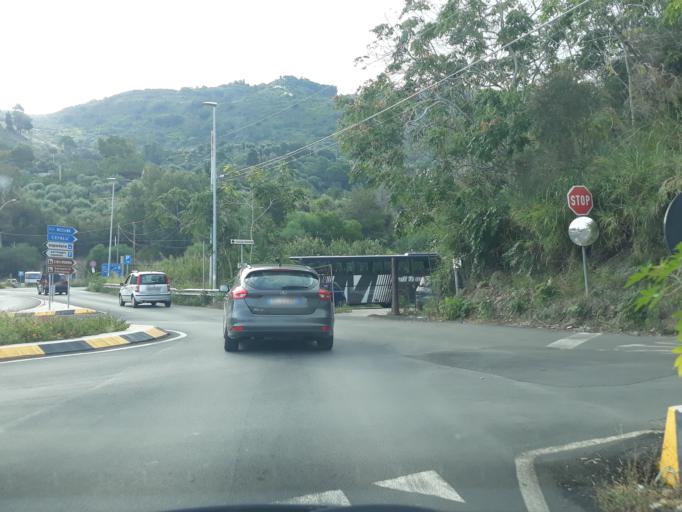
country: IT
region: Sicily
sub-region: Palermo
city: Cefalu
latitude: 38.0267
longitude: 14.0137
